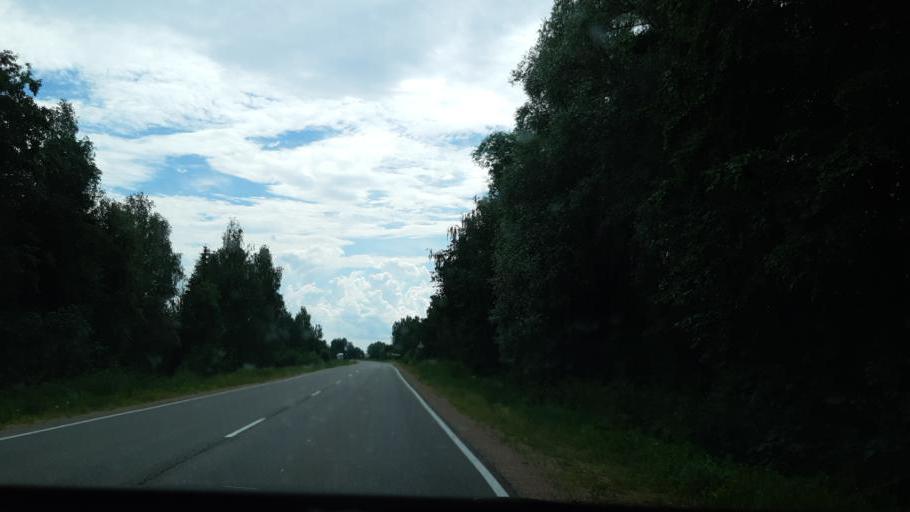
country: RU
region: Kaluga
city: Medyn'
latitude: 55.1200
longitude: 35.9618
